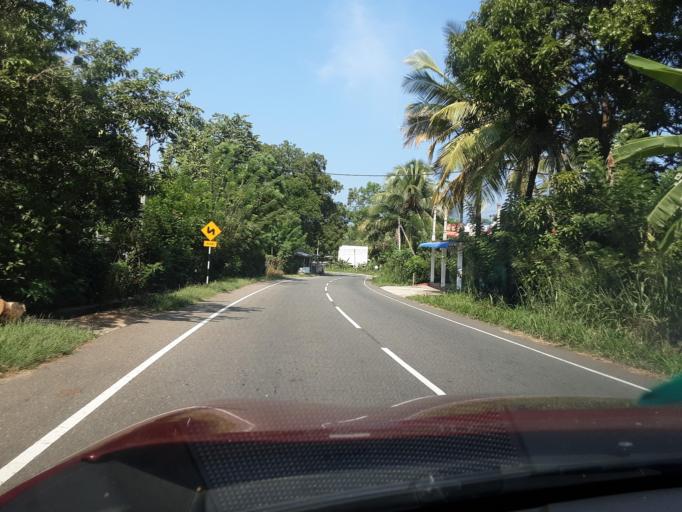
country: LK
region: Uva
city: Badulla
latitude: 7.1901
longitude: 81.0332
